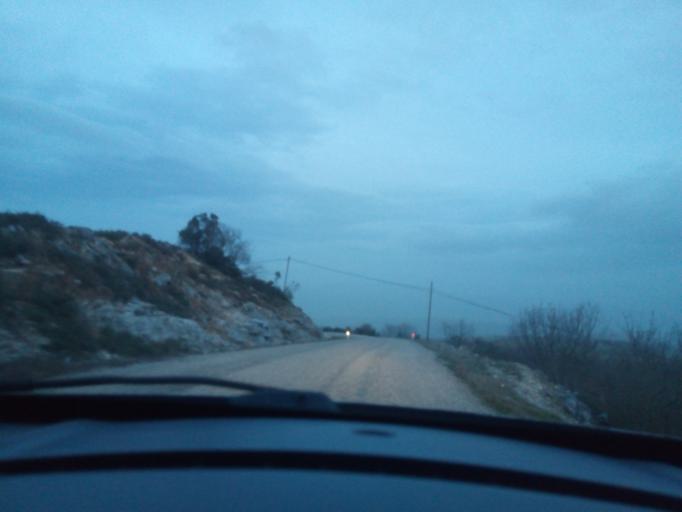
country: TR
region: Balikesir
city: Omerkoy
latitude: 39.9143
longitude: 28.0510
